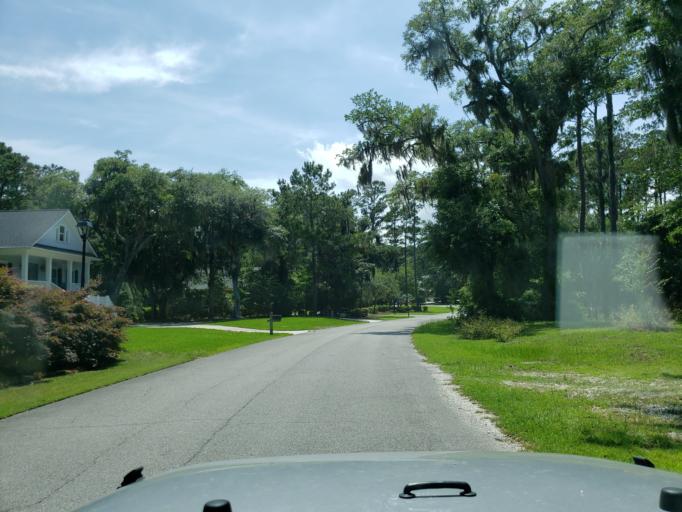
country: US
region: Georgia
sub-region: Chatham County
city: Whitemarsh Island
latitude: 32.0209
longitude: -81.0115
